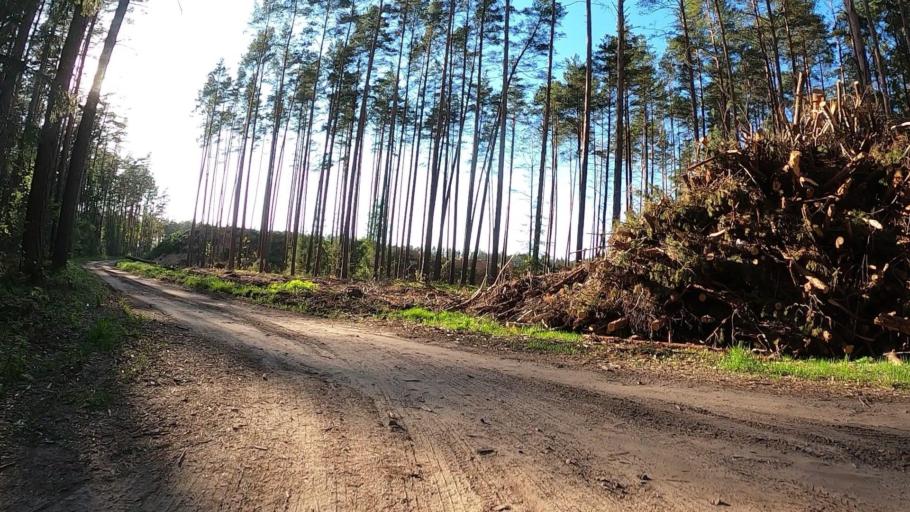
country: LV
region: Baldone
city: Baldone
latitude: 56.7805
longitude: 24.3115
